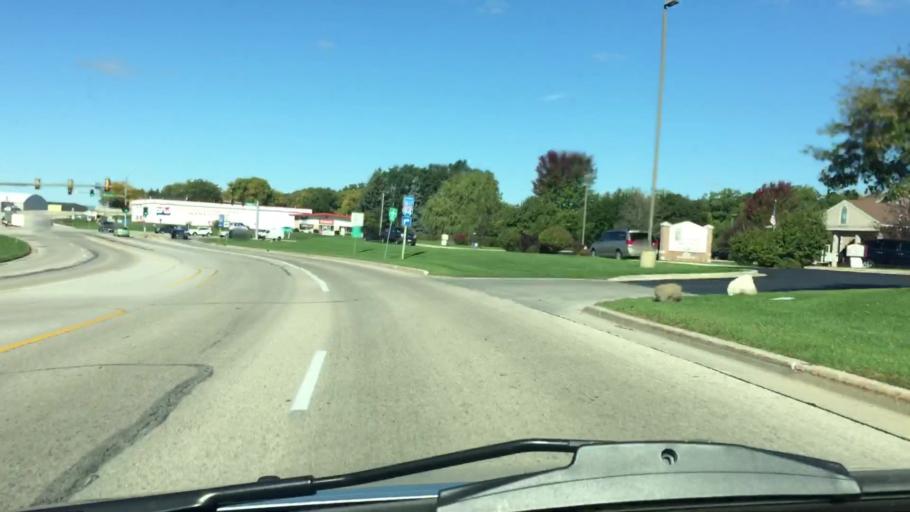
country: US
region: Wisconsin
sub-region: Waukesha County
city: Waukesha
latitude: 43.0416
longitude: -88.2238
